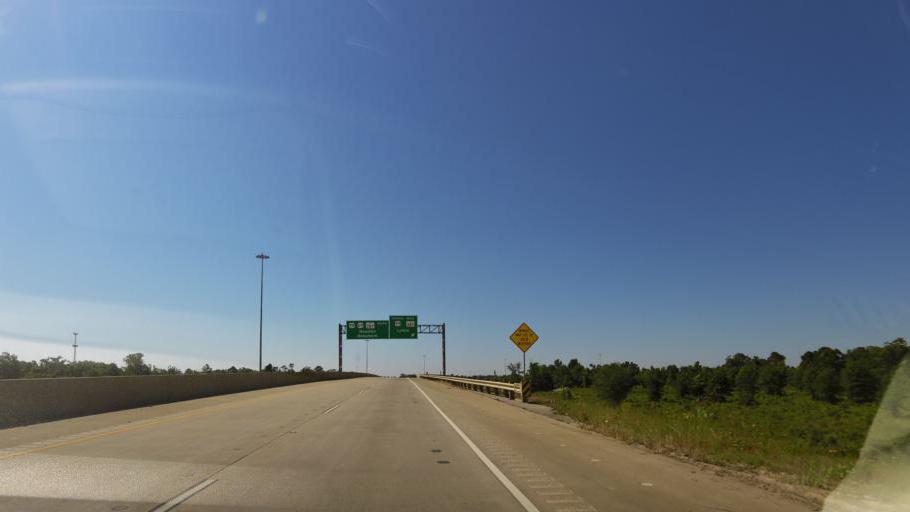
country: US
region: Texas
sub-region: Angelina County
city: Redland
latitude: 31.3770
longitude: -94.7110
